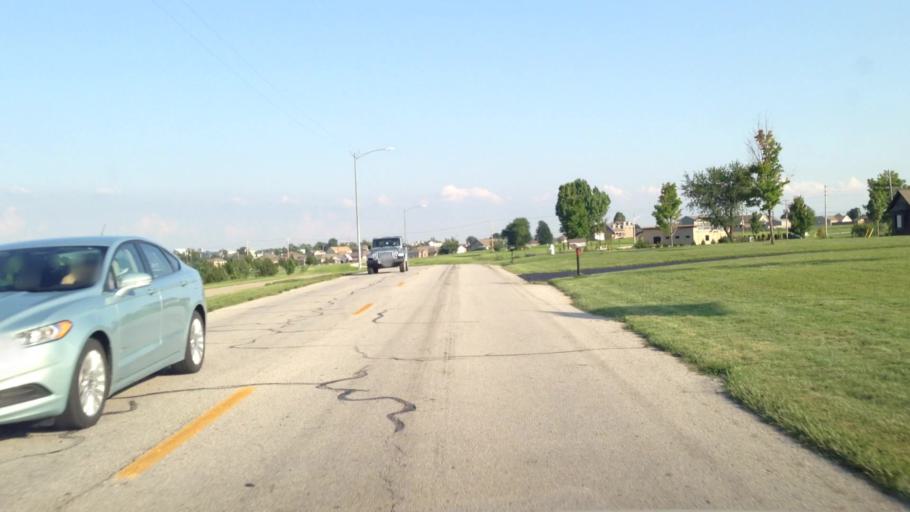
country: US
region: Missouri
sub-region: Jasper County
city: Duquesne
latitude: 37.0718
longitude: -94.4875
